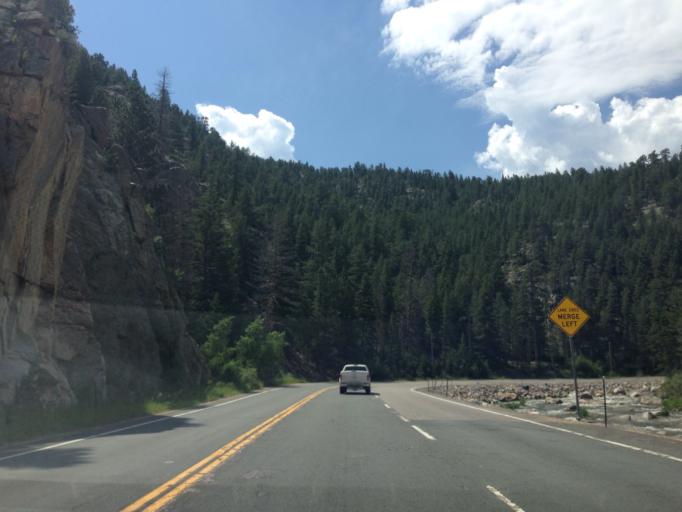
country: US
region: Colorado
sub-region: Larimer County
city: Estes Park
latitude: 40.3962
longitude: -105.4208
